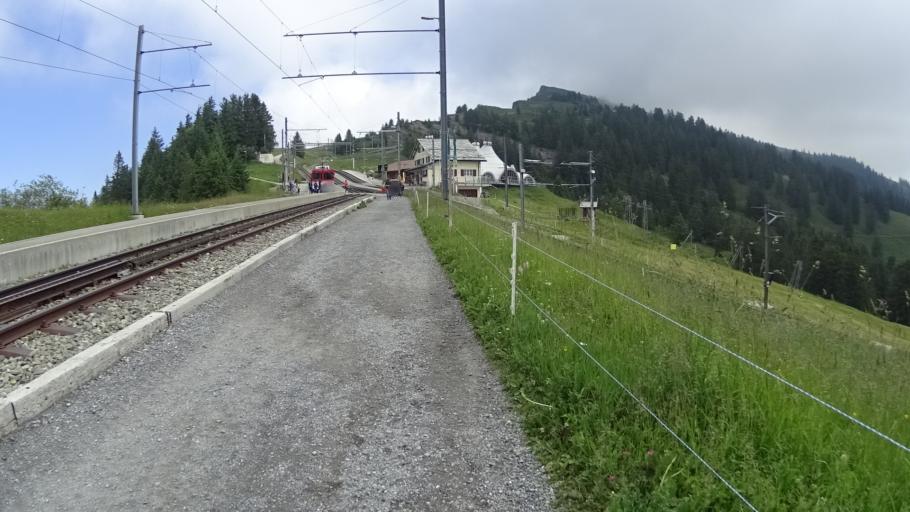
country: CH
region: Lucerne
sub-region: Lucerne-Land District
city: Vitznau
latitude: 47.0529
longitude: 8.4730
